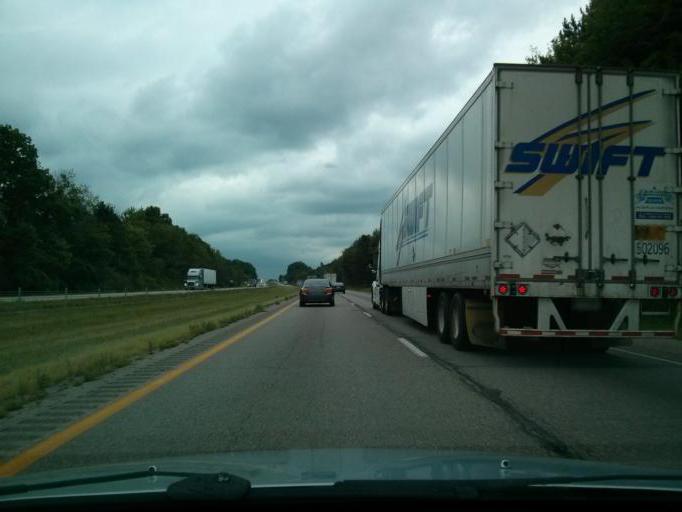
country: US
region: Ohio
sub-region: Portage County
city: Ravenna
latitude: 41.1057
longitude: -81.1806
